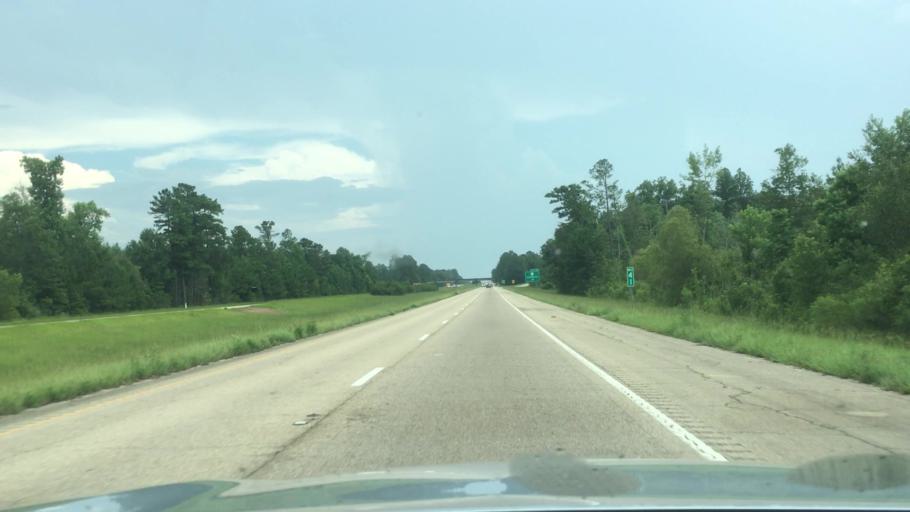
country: US
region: Mississippi
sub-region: Lamar County
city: Lumberton
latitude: 30.9941
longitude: -89.4219
